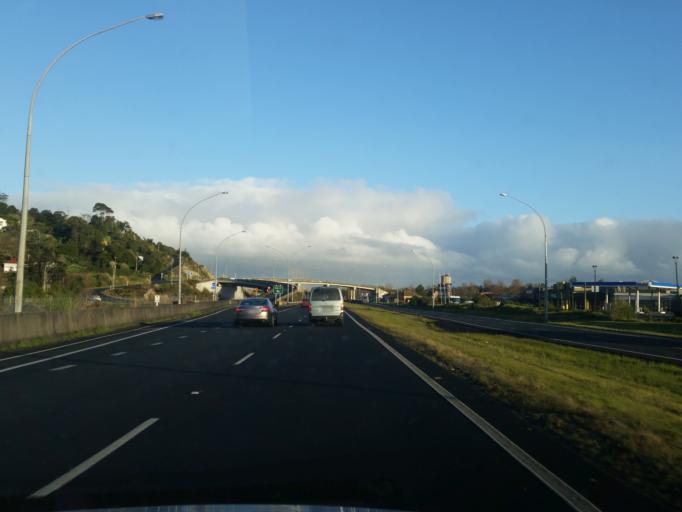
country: NZ
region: Auckland
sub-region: Auckland
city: Pukekohe East
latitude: -37.2764
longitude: 175.0471
